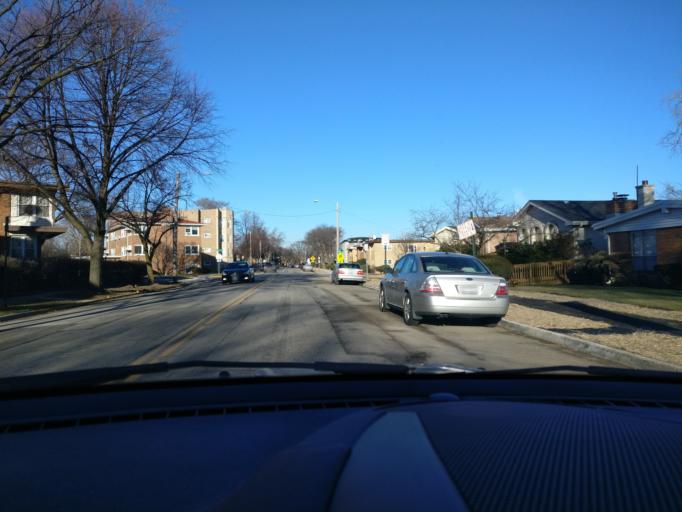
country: US
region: Illinois
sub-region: Cook County
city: Skokie
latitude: 42.0457
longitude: -87.7446
